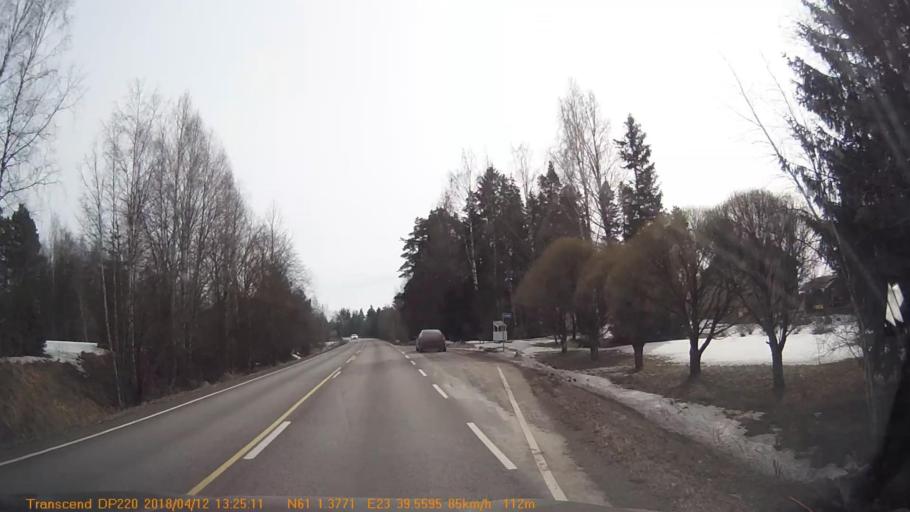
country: FI
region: Pirkanmaa
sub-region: Etelae-Pirkanmaa
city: Kylmaekoski
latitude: 61.0228
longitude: 23.6595
